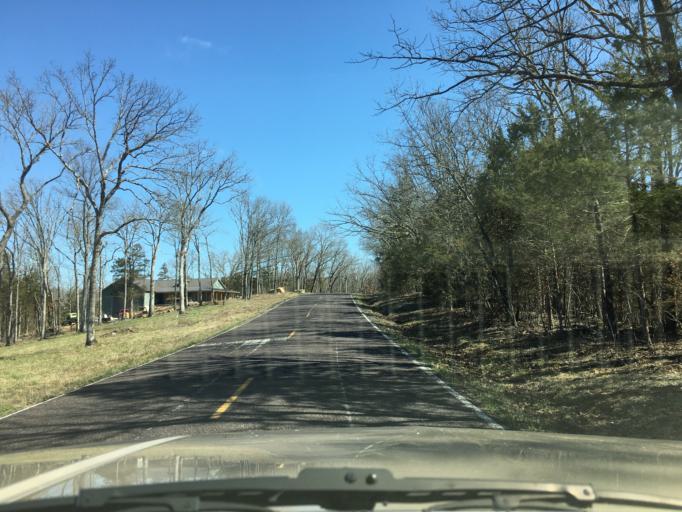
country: US
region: Missouri
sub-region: Franklin County
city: New Haven
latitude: 38.5356
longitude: -91.3312
